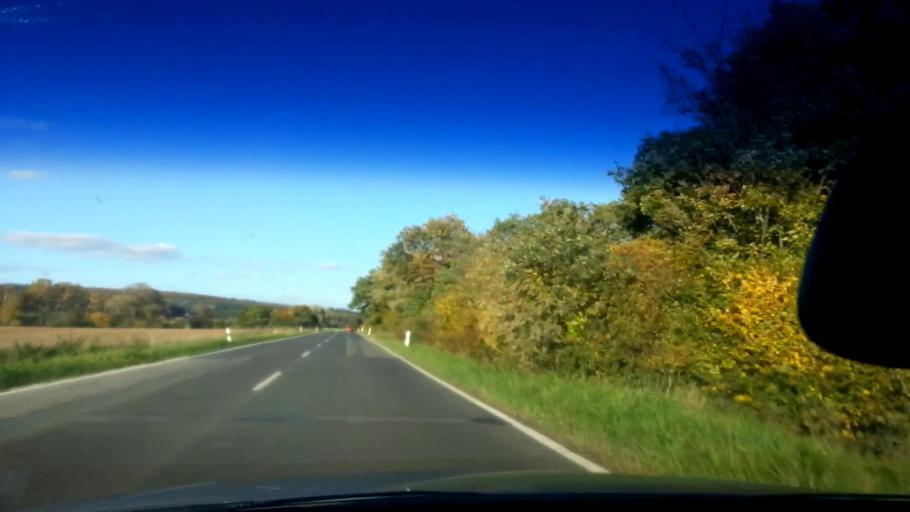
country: DE
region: Bavaria
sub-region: Upper Franconia
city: Zapfendorf
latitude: 50.0309
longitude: 10.9113
